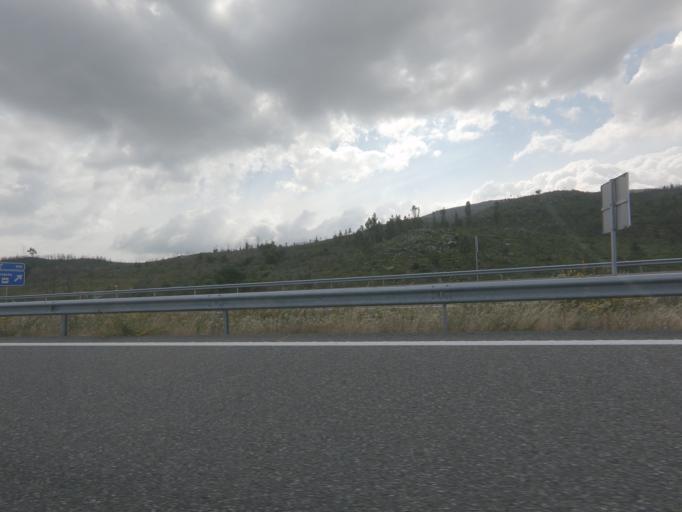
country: ES
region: Galicia
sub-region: Provincia de Ourense
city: Melon
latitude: 42.2767
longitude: -8.2031
